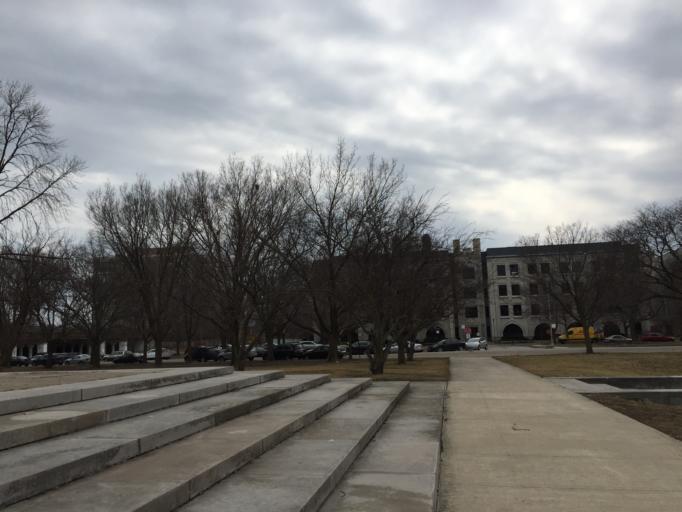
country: US
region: Illinois
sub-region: Cook County
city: Chicago
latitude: 41.7870
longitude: -87.5903
